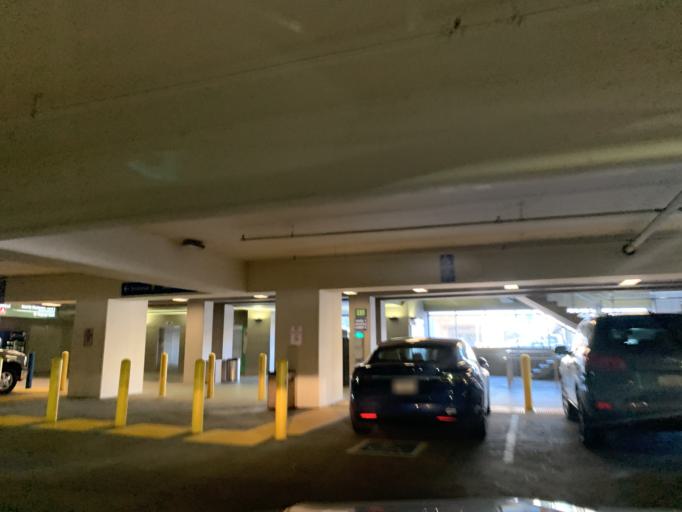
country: US
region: California
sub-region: Yolo County
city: West Sacramento
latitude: 38.6922
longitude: -121.5882
